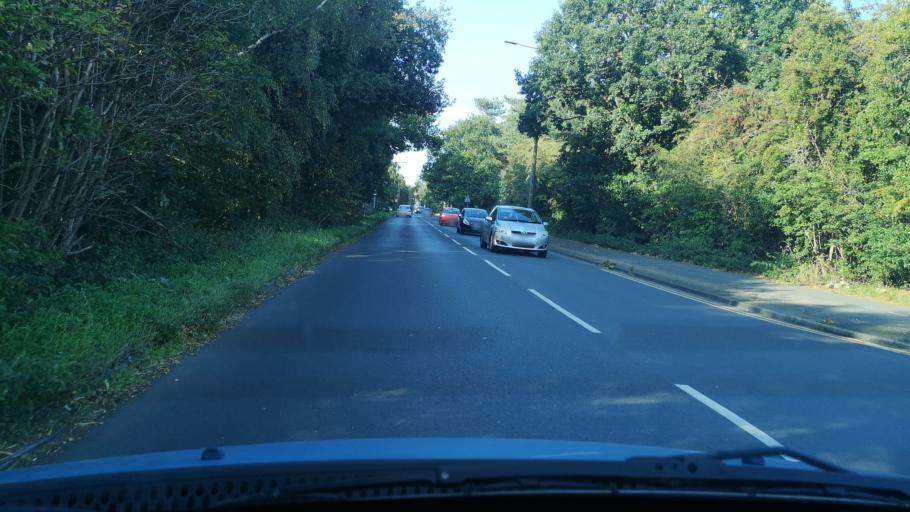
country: GB
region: England
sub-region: North Lincolnshire
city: Scunthorpe
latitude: 53.5806
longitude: -0.6840
